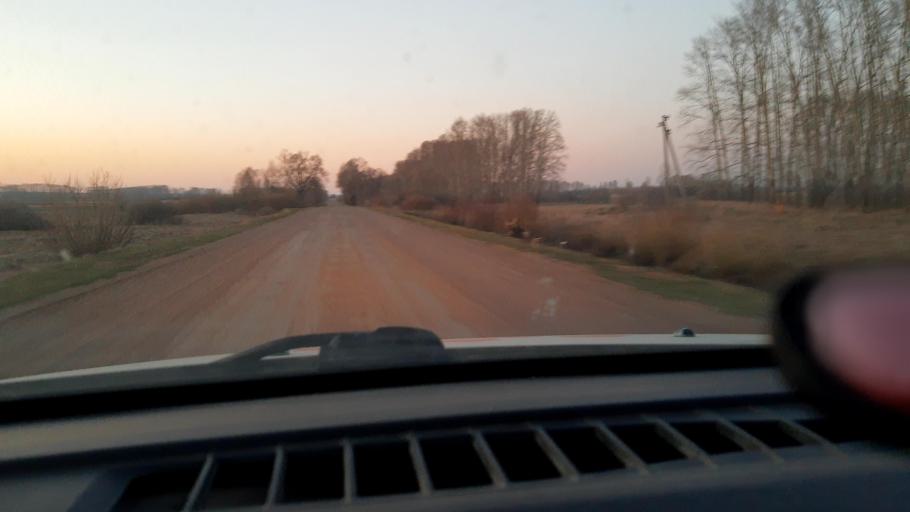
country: RU
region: Bashkortostan
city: Asanovo
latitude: 54.8594
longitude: 55.4606
